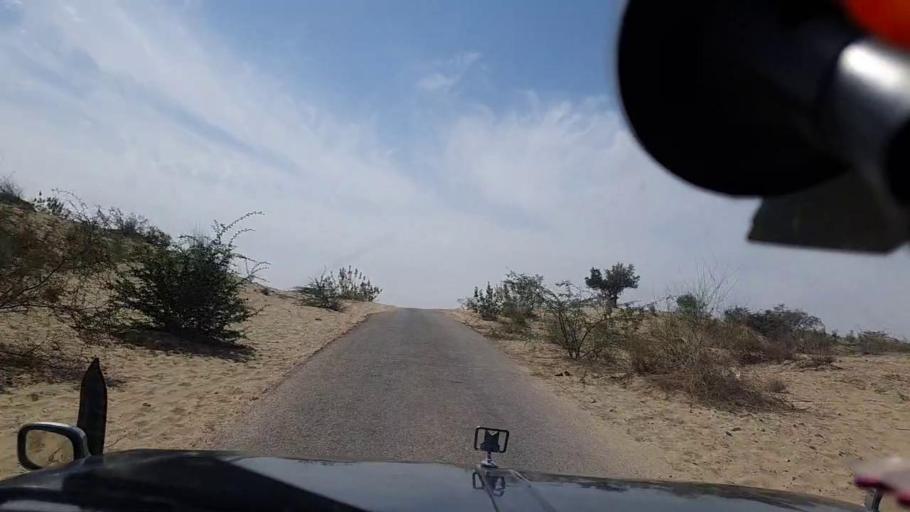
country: PK
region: Sindh
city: Diplo
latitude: 24.4226
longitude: 69.5829
